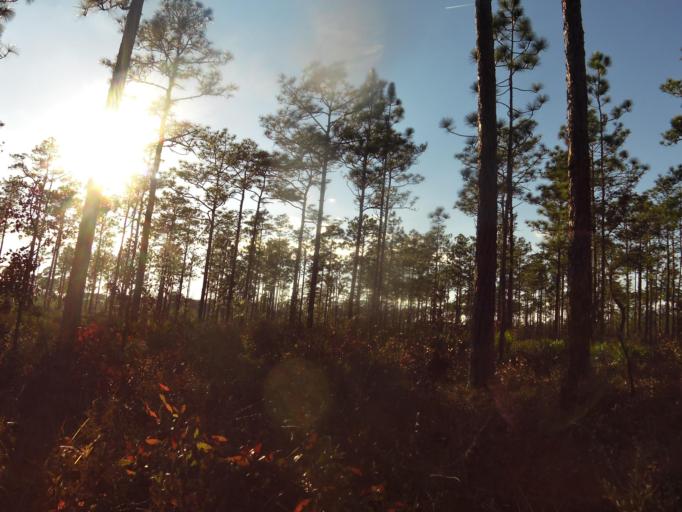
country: US
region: Florida
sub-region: Clay County
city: Middleburg
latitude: 30.1402
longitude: -81.9595
